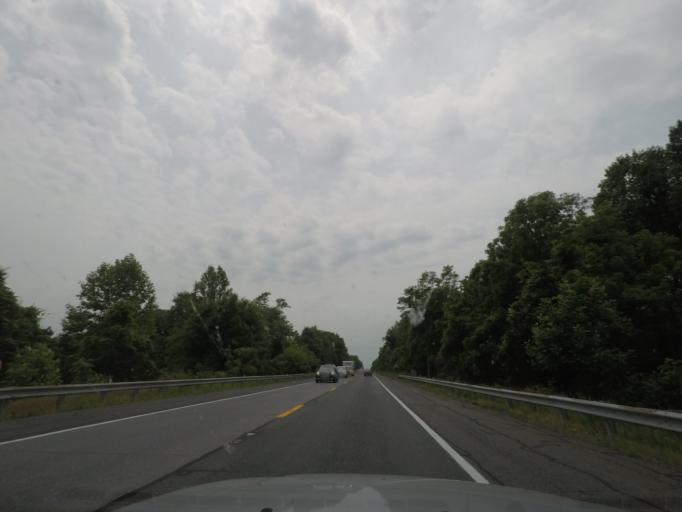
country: US
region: Maryland
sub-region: Frederick County
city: Jefferson
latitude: 39.3300
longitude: -77.5104
